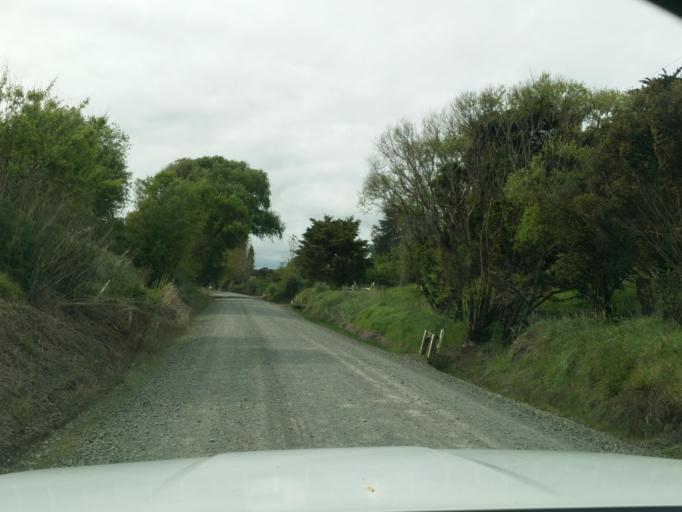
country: NZ
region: Northland
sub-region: Kaipara District
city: Dargaville
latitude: -35.9090
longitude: 173.9226
